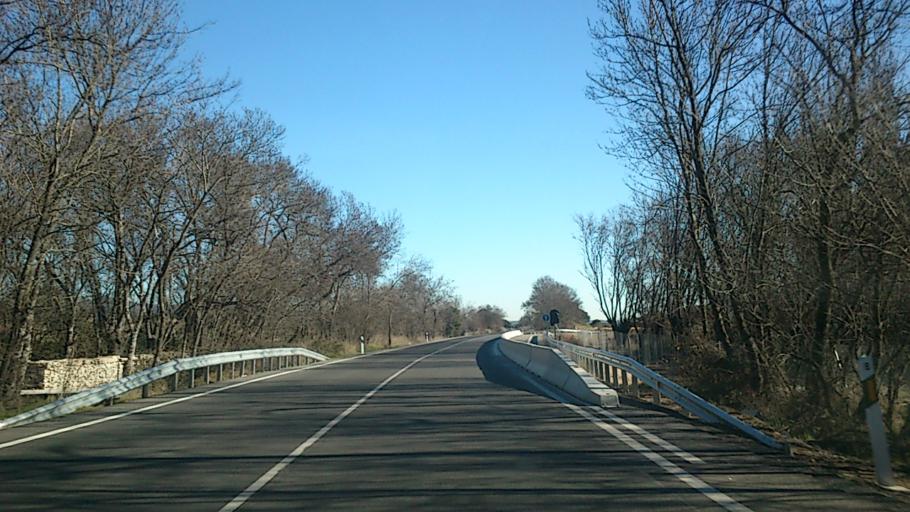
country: ES
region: Madrid
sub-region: Provincia de Madrid
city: Alpedrete
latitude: 40.6518
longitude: -4.0567
